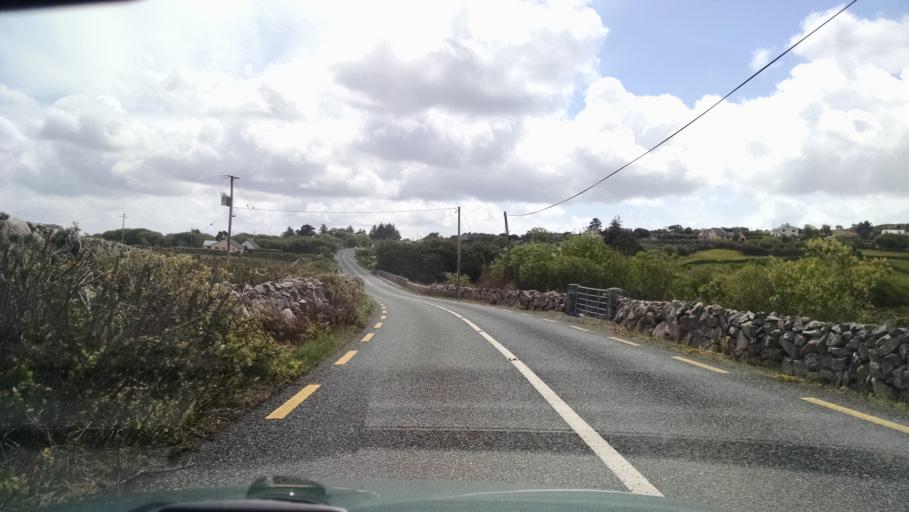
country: IE
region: Connaught
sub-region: County Galway
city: Clifden
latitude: 53.3577
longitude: -9.7043
